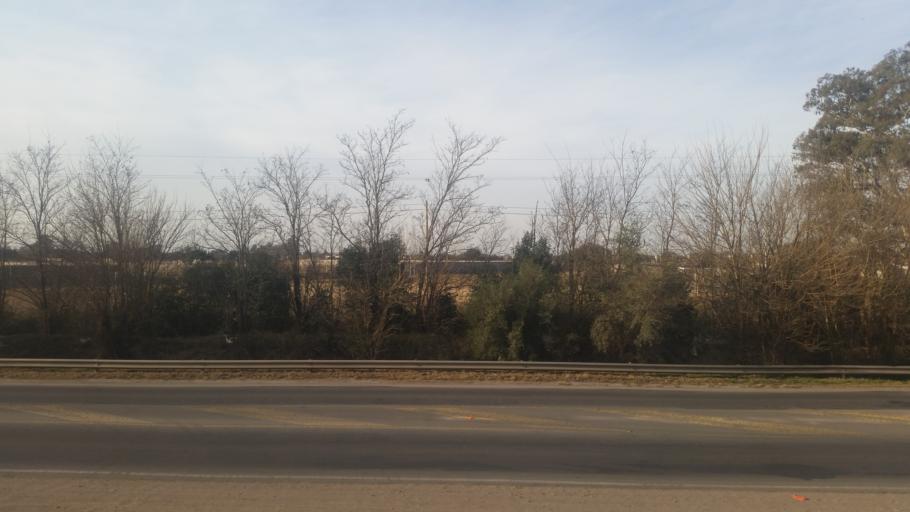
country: AR
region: Cordoba
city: Malvinas Argentinas
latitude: -31.4764
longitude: -64.0914
